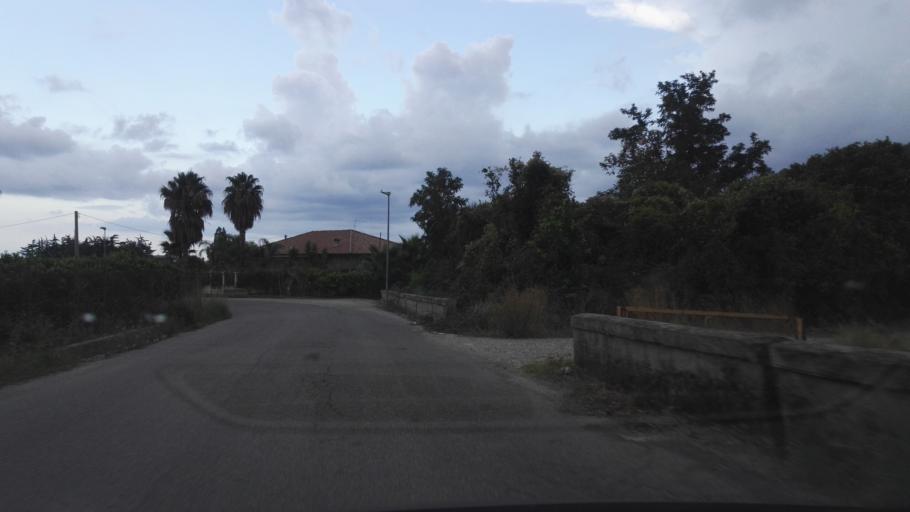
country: IT
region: Calabria
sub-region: Provincia di Reggio Calabria
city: Caulonia Marina
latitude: 38.3601
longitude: 16.4662
